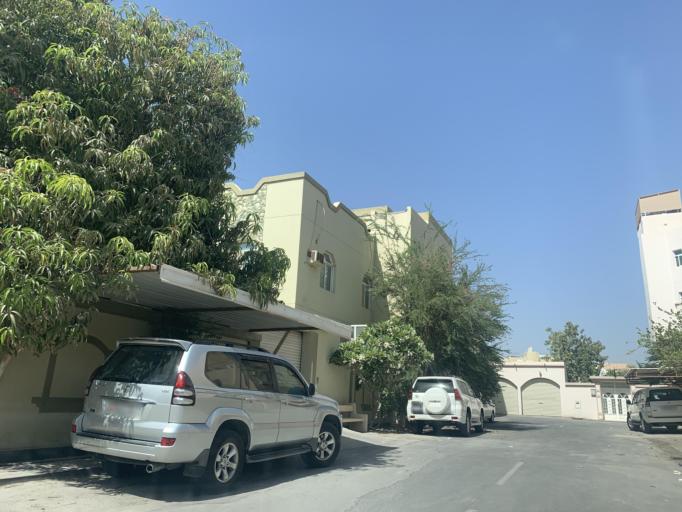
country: BH
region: Manama
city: Jidd Hafs
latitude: 26.2254
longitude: 50.5311
